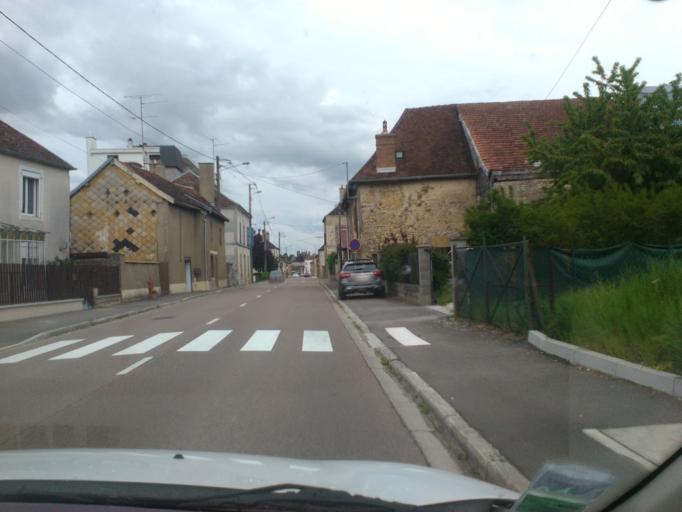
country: FR
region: Champagne-Ardenne
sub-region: Departement de l'Aube
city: Vendeuvre-sur-Barse
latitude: 48.2361
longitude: 4.4604
